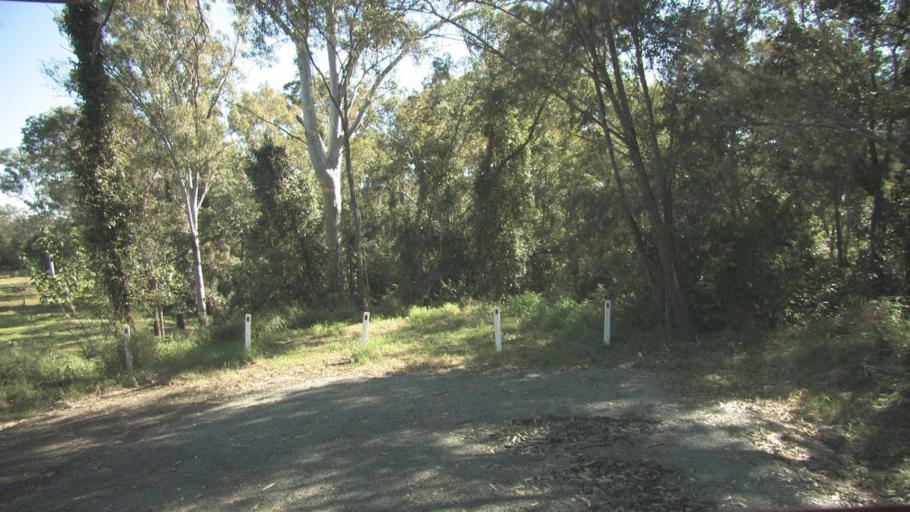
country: AU
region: Queensland
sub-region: Logan
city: Chambers Flat
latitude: -27.7599
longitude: 153.1153
